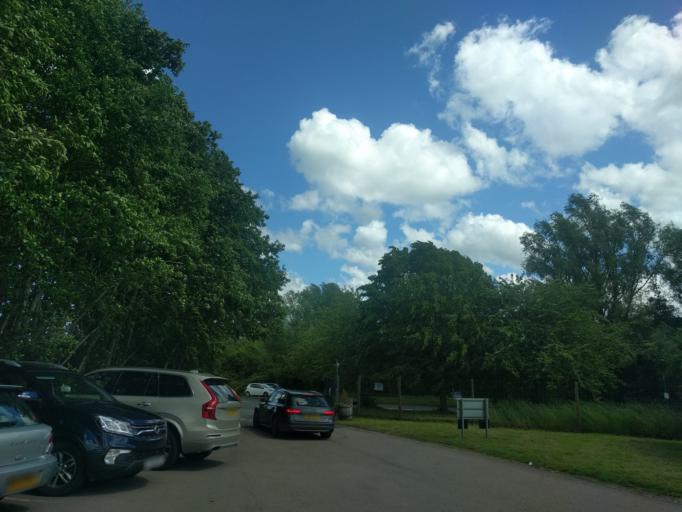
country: GB
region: England
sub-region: Wiltshire
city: Chilton Foliat
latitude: 51.4150
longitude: -1.5416
